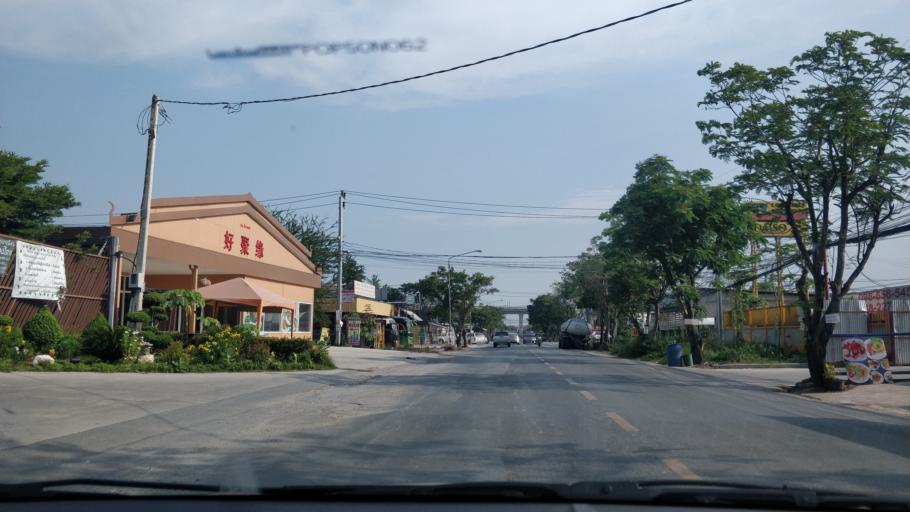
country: TH
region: Bangkok
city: Saphan Sung
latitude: 13.7350
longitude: 100.7162
